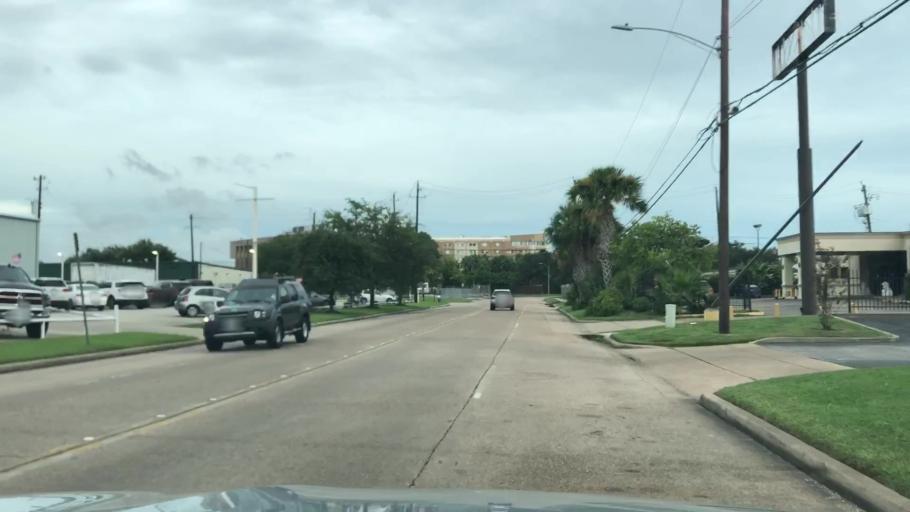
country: US
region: Texas
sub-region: Harris County
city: Bellaire
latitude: 29.7179
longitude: -95.4966
